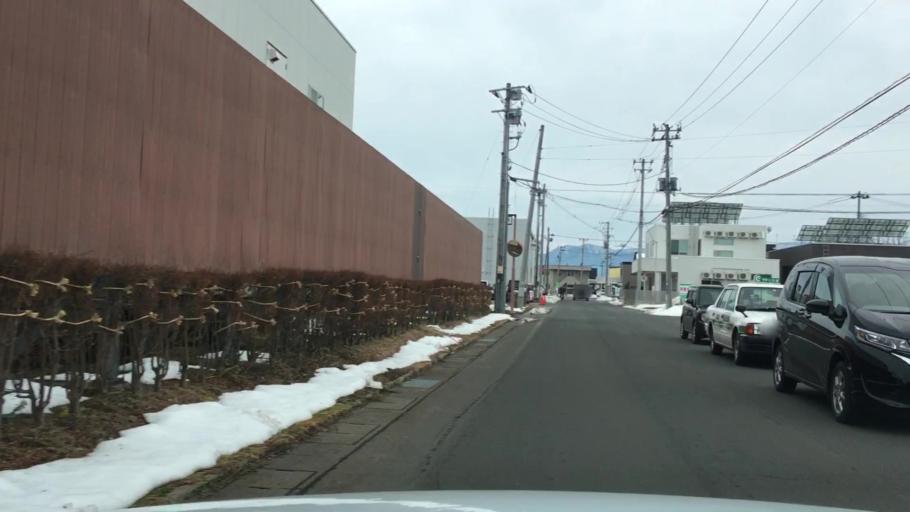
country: JP
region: Aomori
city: Hirosaki
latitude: 40.6015
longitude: 140.5129
